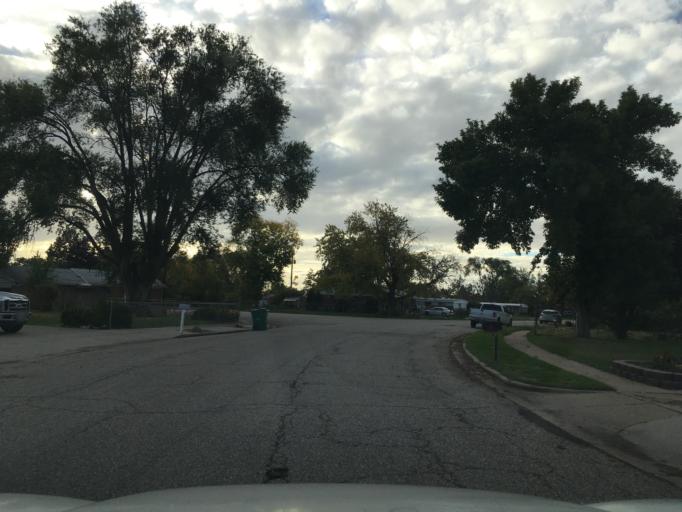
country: US
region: Utah
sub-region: Davis County
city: Layton
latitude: 41.0787
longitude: -111.9905
